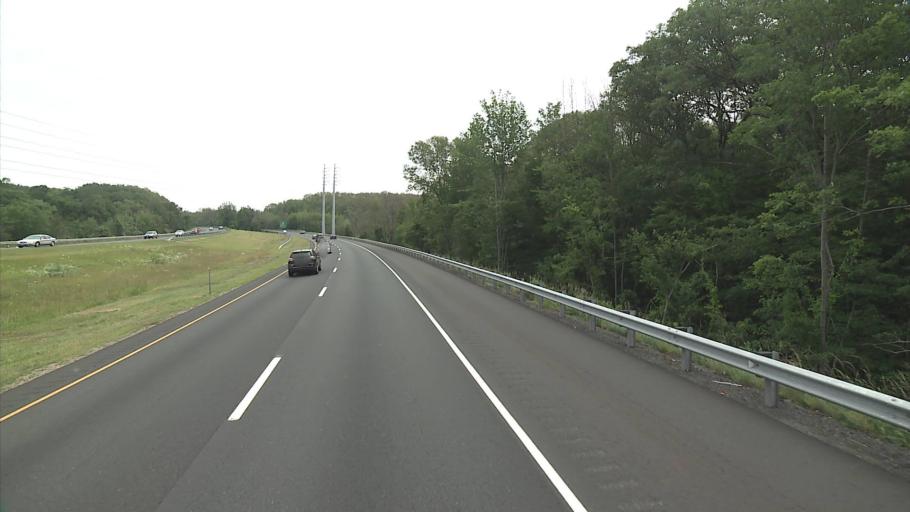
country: US
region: Connecticut
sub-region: New Haven County
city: Middlebury
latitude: 41.5235
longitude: -73.0903
